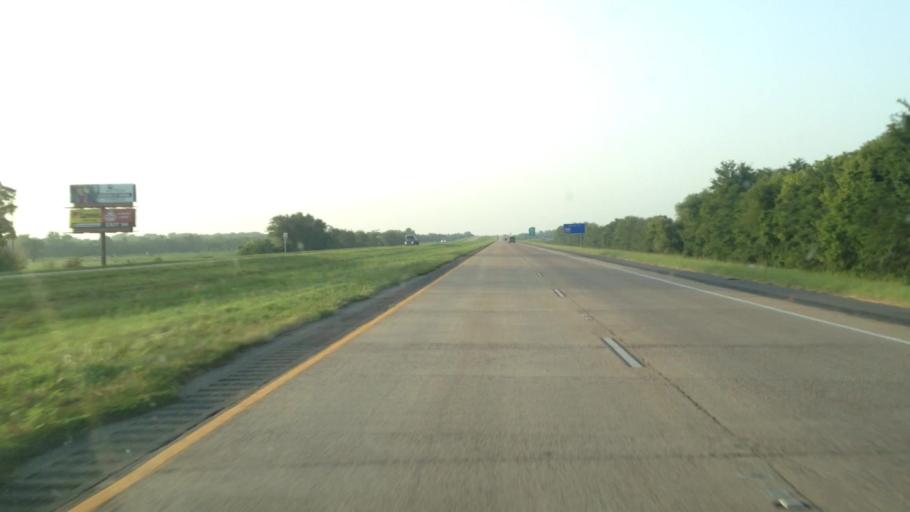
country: US
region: Louisiana
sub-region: Natchitoches Parish
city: Vienna Bend
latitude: 31.6184
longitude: -93.0585
